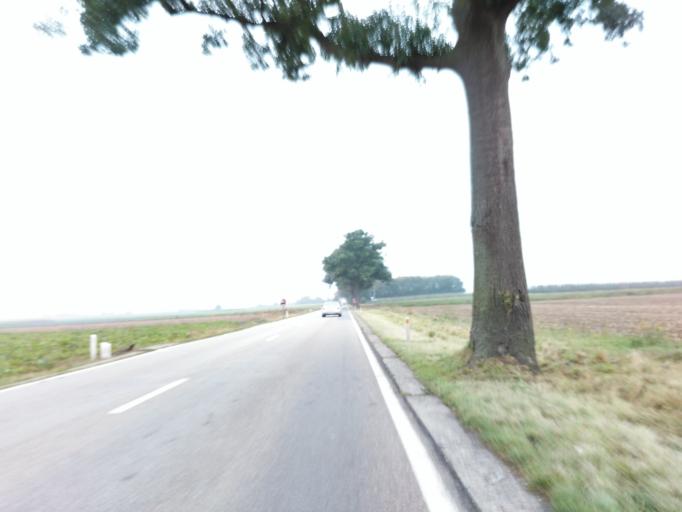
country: BE
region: Flanders
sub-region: Provincie Limburg
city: Riemst
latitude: 50.8609
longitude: 5.6050
